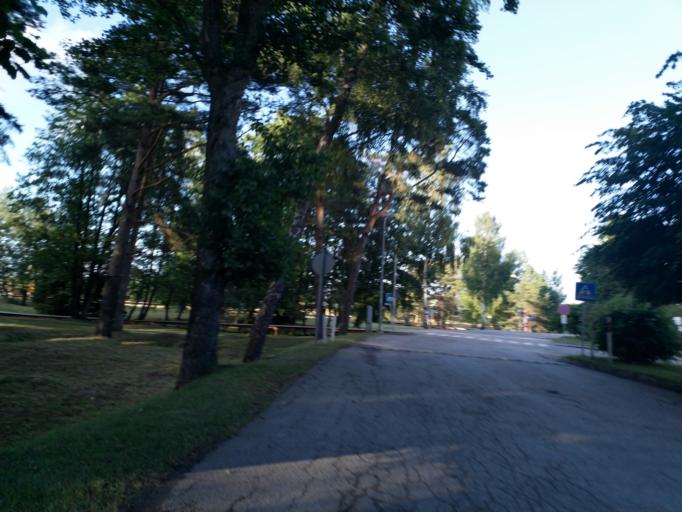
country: LV
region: Rojas
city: Roja
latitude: 57.5094
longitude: 22.8006
